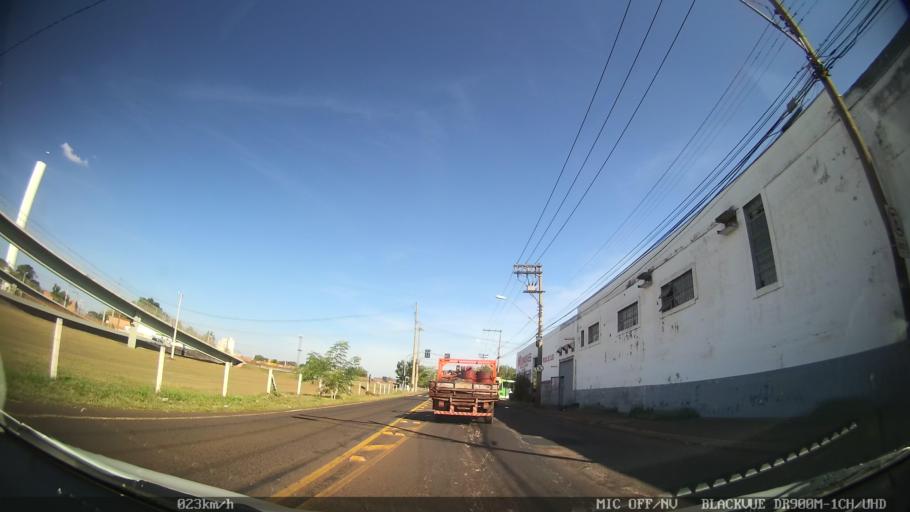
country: BR
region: Sao Paulo
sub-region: Ribeirao Preto
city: Ribeirao Preto
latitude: -21.1839
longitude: -47.7577
